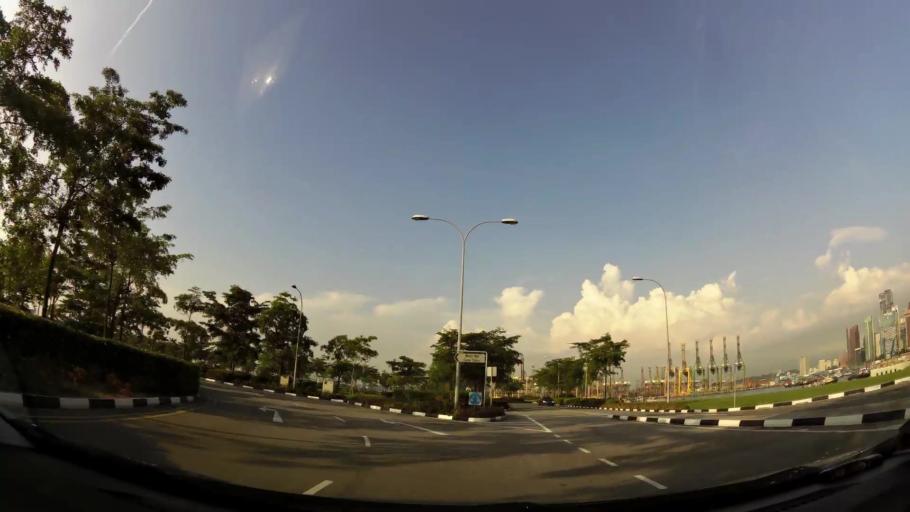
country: SG
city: Singapore
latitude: 1.2691
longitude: 103.8591
